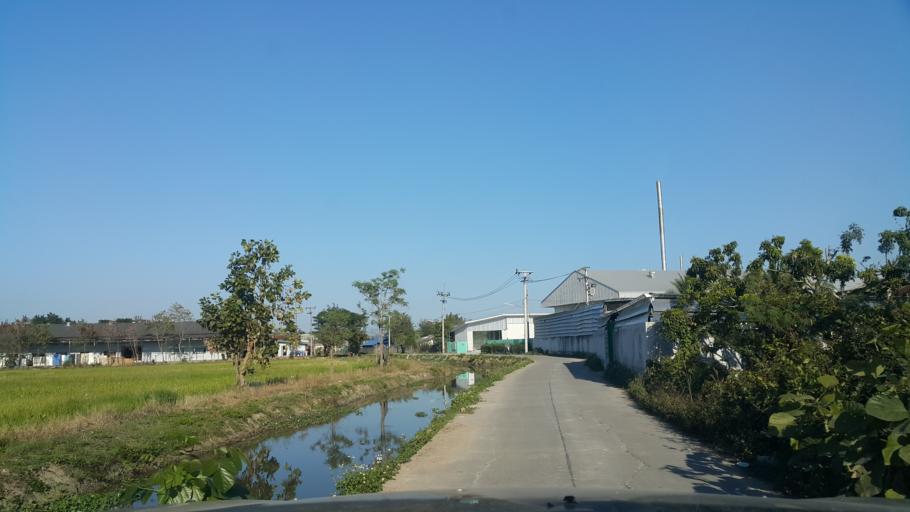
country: TH
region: Chiang Mai
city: Hang Dong
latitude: 18.6812
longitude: 98.9722
